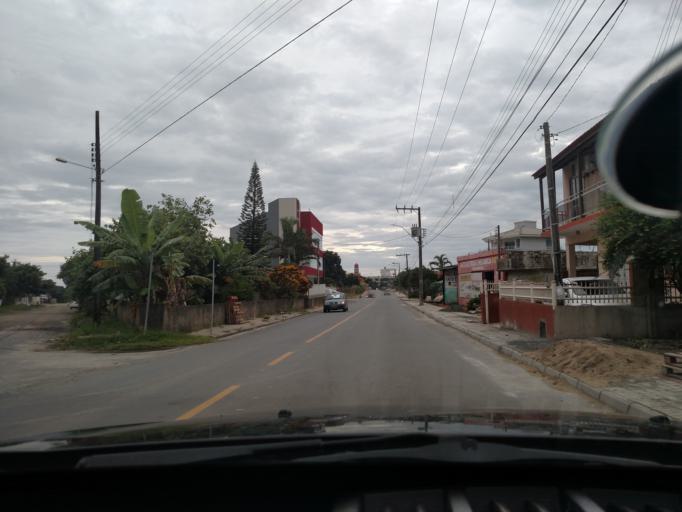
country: BR
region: Santa Catarina
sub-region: Porto Belo
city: Porto Belo
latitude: -27.1541
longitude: -48.5116
